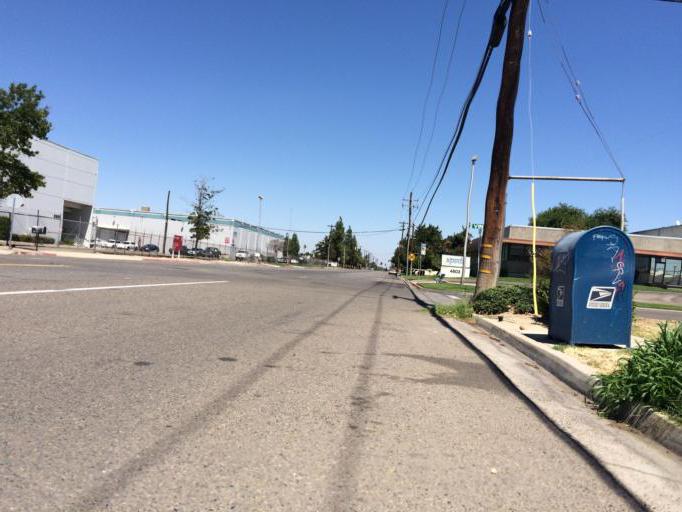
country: US
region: California
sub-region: Fresno County
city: Fresno
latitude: 36.7030
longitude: -119.7456
